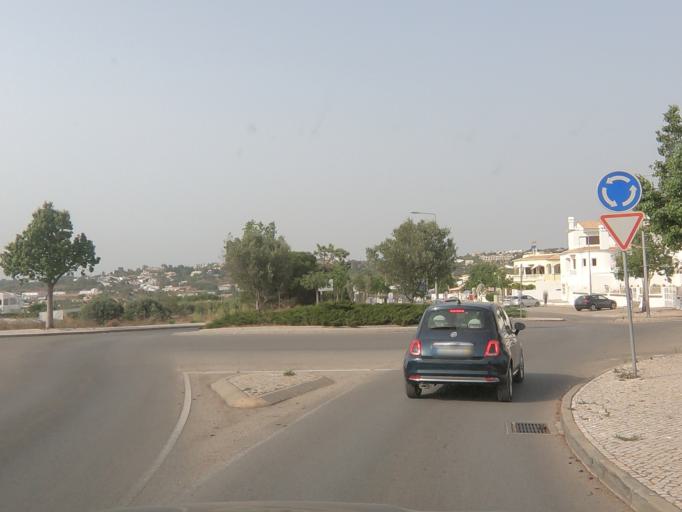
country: PT
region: Faro
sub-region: Albufeira
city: Guia
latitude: 37.0818
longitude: -8.2981
